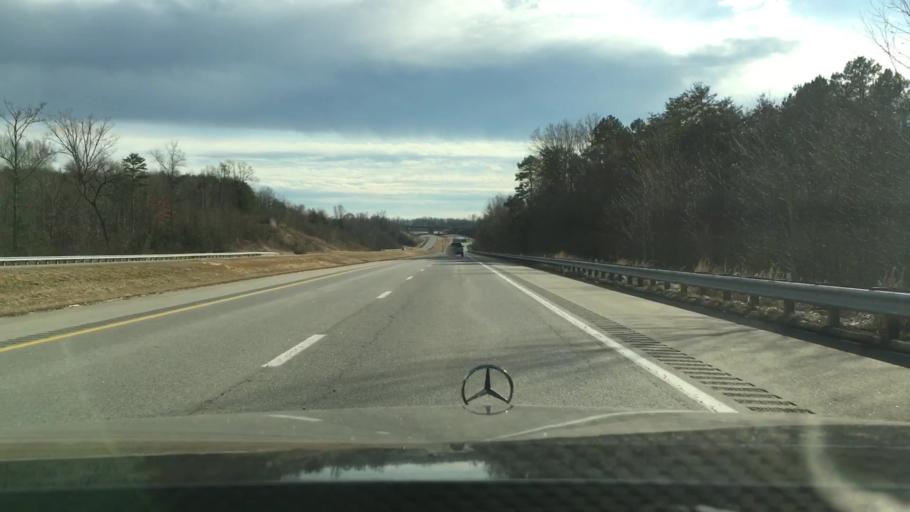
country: US
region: Virginia
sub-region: City of Danville
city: Danville
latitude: 36.6267
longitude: -79.3651
